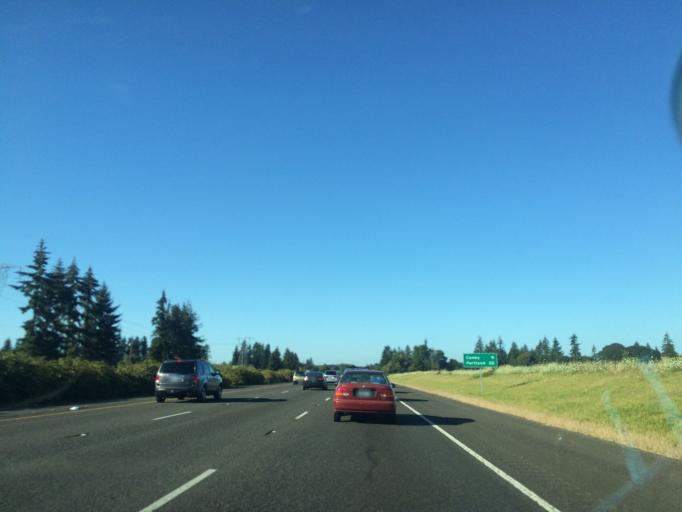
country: US
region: Oregon
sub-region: Clackamas County
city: Wilsonville
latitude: 45.2476
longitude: -122.7960
